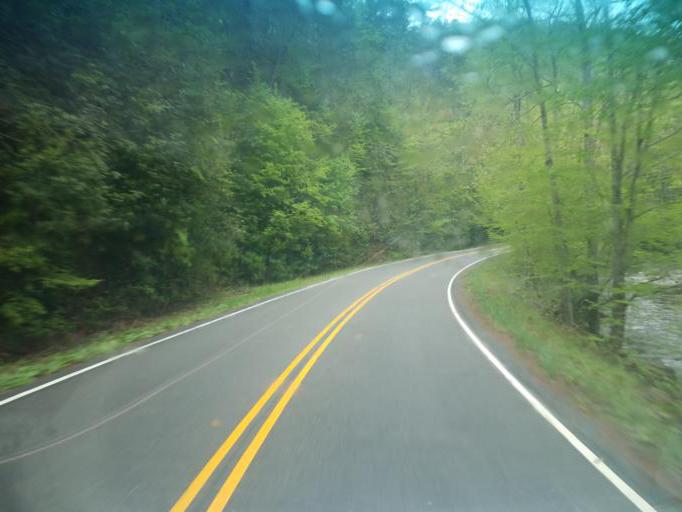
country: US
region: Tennessee
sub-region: Johnson County
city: Mountain City
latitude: 36.6272
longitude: -81.7566
